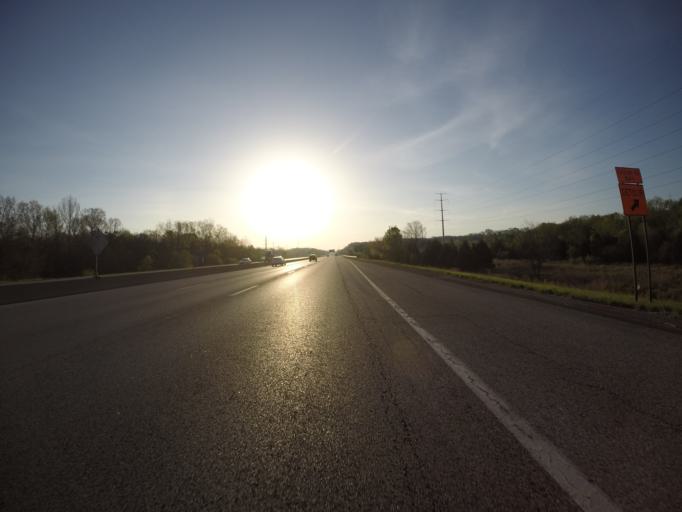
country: US
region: Missouri
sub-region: Jackson County
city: Raytown
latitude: 38.9366
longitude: -94.4547
